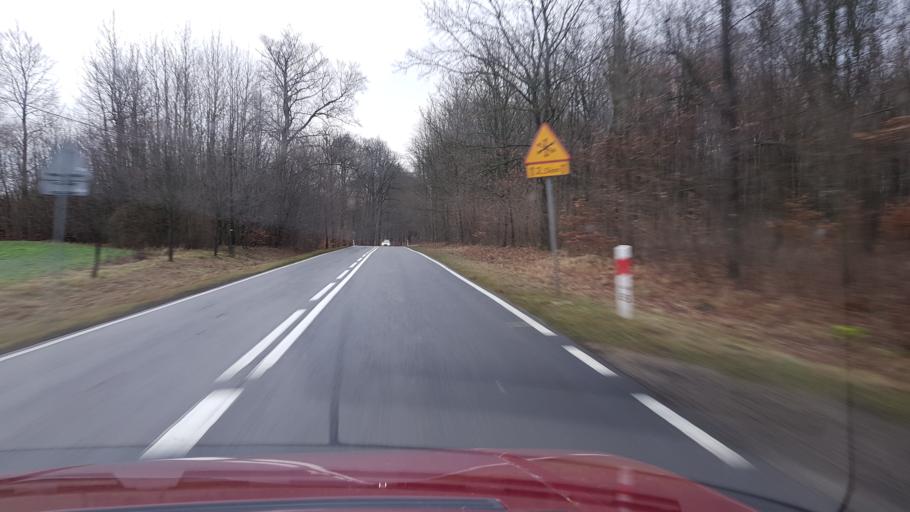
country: PL
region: West Pomeranian Voivodeship
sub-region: Powiat lobeski
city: Wegorzyno
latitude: 53.5254
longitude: 15.5939
